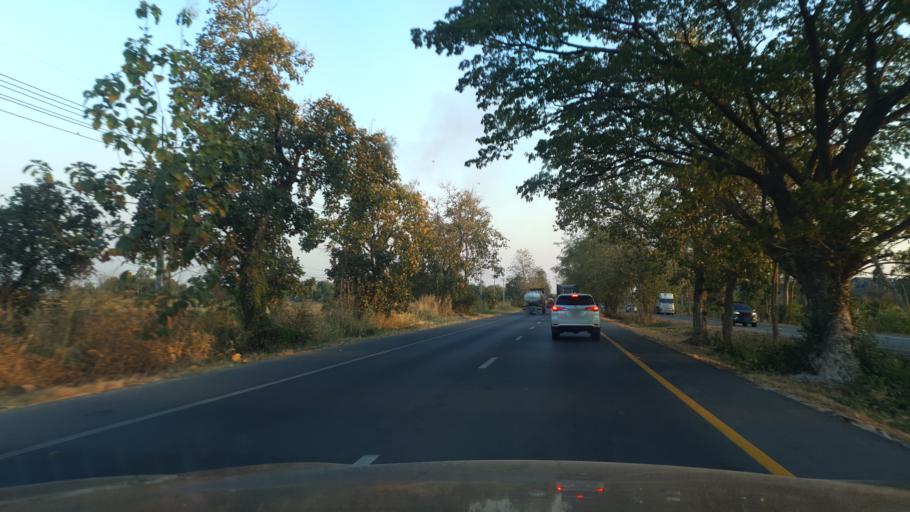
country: TH
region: Nakhon Sawan
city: Banphot Phisai
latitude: 15.8698
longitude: 99.9122
